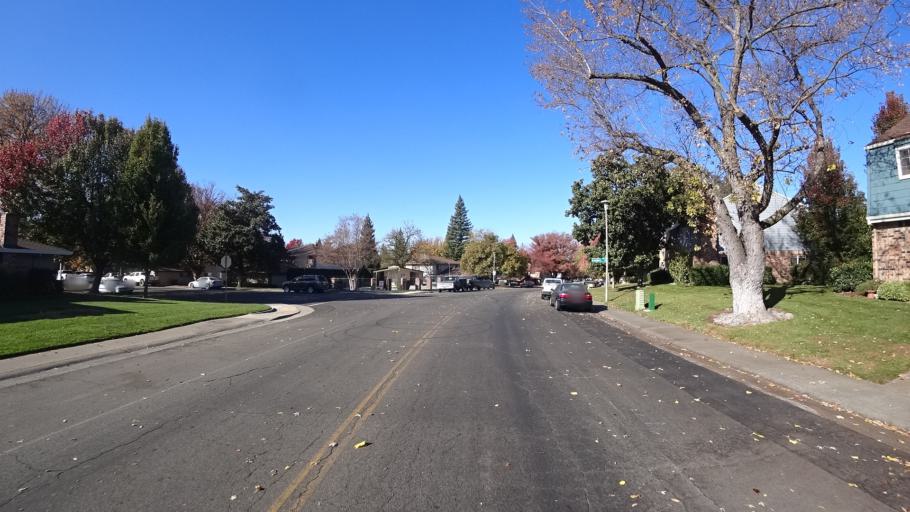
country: US
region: California
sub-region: Sacramento County
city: Antelope
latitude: 38.6816
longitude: -121.3132
